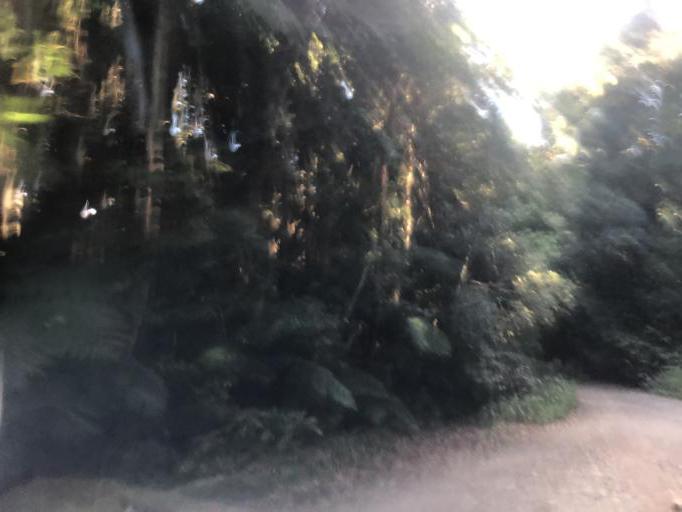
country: AU
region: New South Wales
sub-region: Coffs Harbour
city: Coffs Harbour
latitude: -30.2403
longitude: 153.0956
